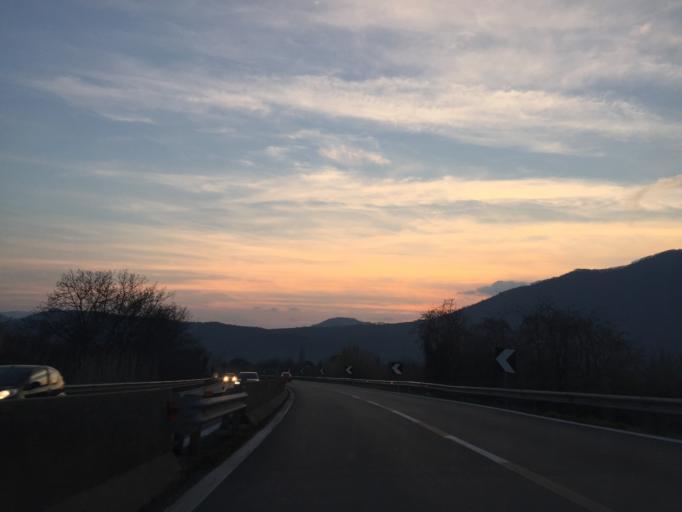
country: IT
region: Campania
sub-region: Provincia di Avellino
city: San Pietro
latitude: 40.8161
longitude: 14.7791
